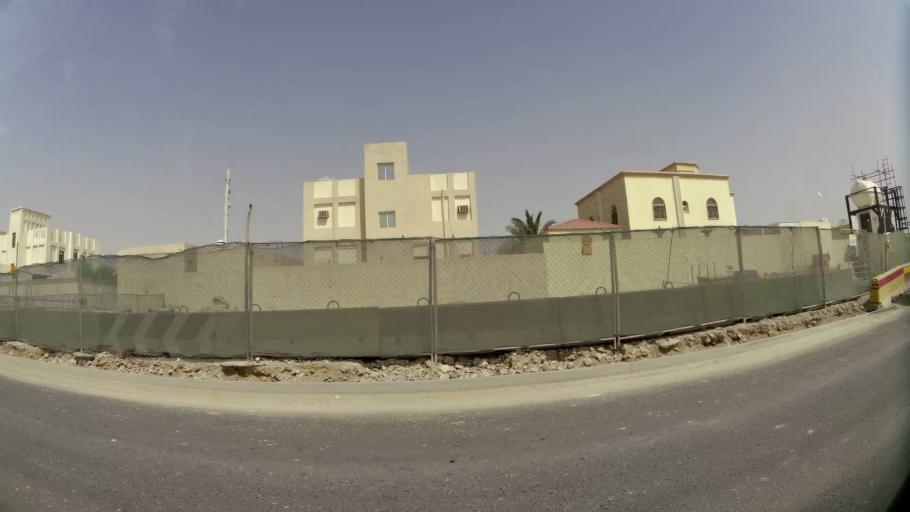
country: QA
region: Baladiyat ar Rayyan
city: Ar Rayyan
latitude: 25.2462
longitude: 51.3625
